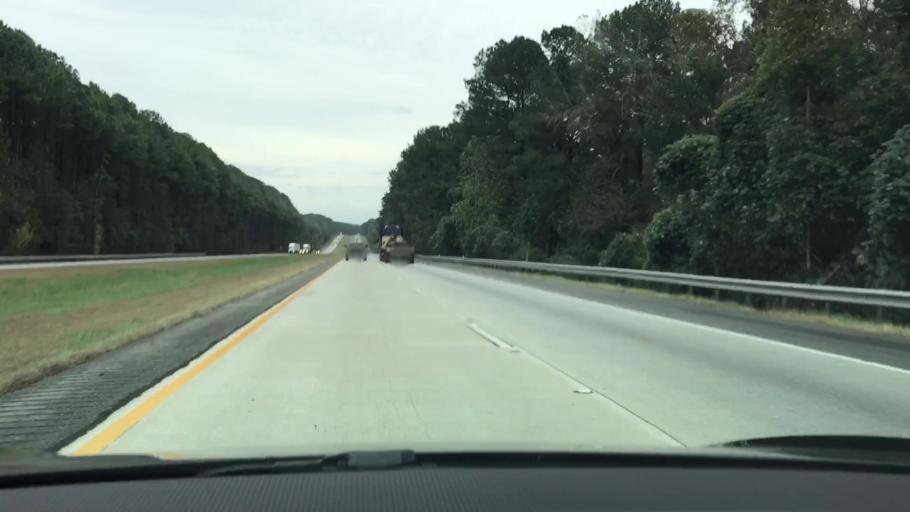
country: US
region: Georgia
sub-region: Greene County
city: Greensboro
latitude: 33.5484
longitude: -83.1545
